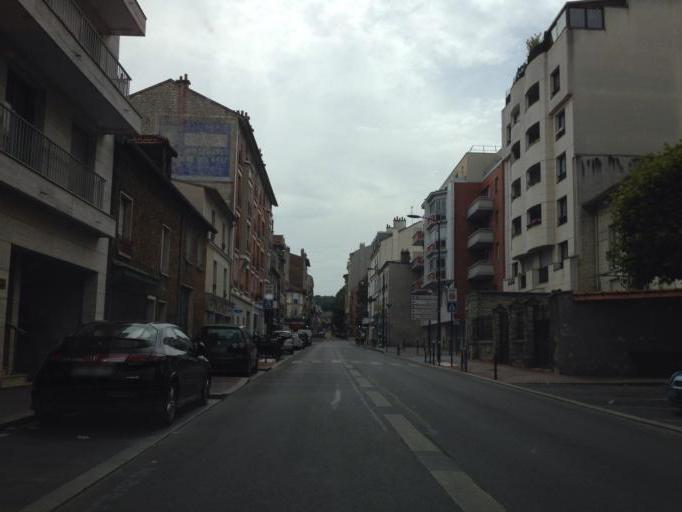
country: FR
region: Ile-de-France
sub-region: Departement des Hauts-de-Seine
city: Clamart
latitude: 48.8049
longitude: 2.2667
